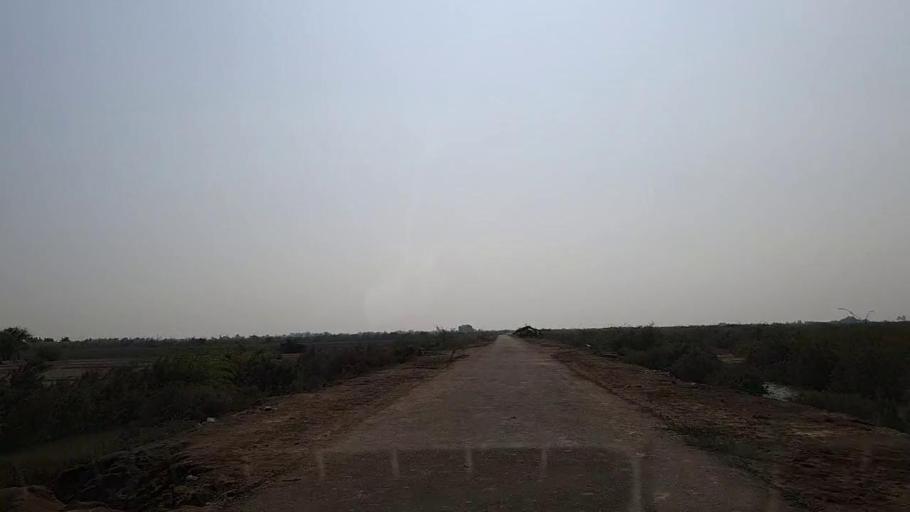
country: PK
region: Sindh
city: Mirpur Sakro
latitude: 24.6584
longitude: 67.6924
